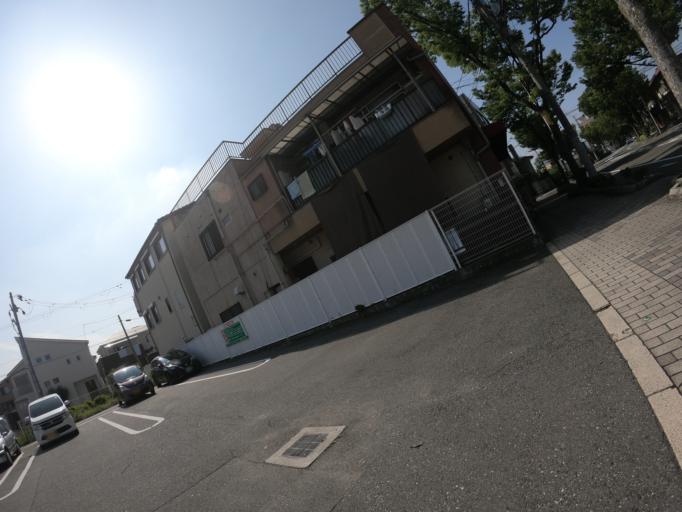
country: JP
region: Osaka
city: Sakai
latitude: 34.5703
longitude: 135.4898
